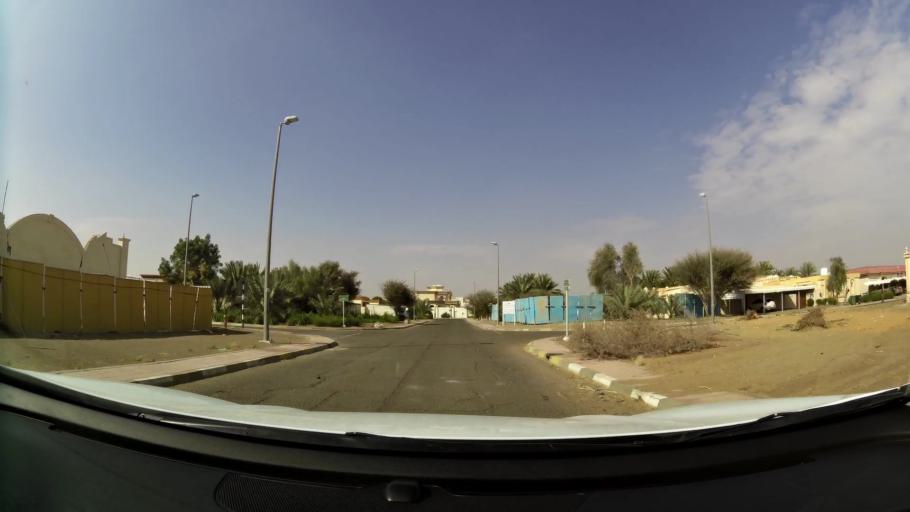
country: AE
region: Abu Dhabi
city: Al Ain
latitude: 24.0974
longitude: 55.9176
